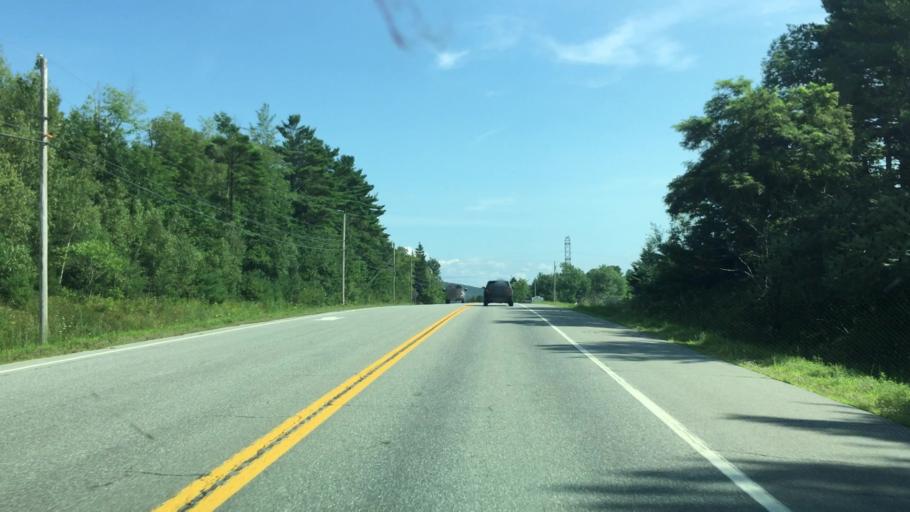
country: US
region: Maine
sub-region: Waldo County
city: Winterport
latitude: 44.6781
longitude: -68.8417
